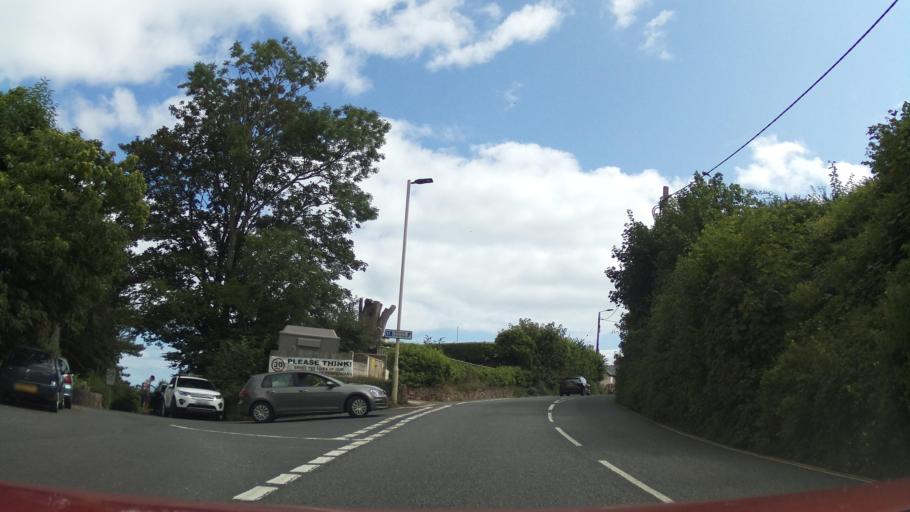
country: GB
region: England
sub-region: Devon
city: Teignmouth
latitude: 50.5381
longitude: -3.5037
